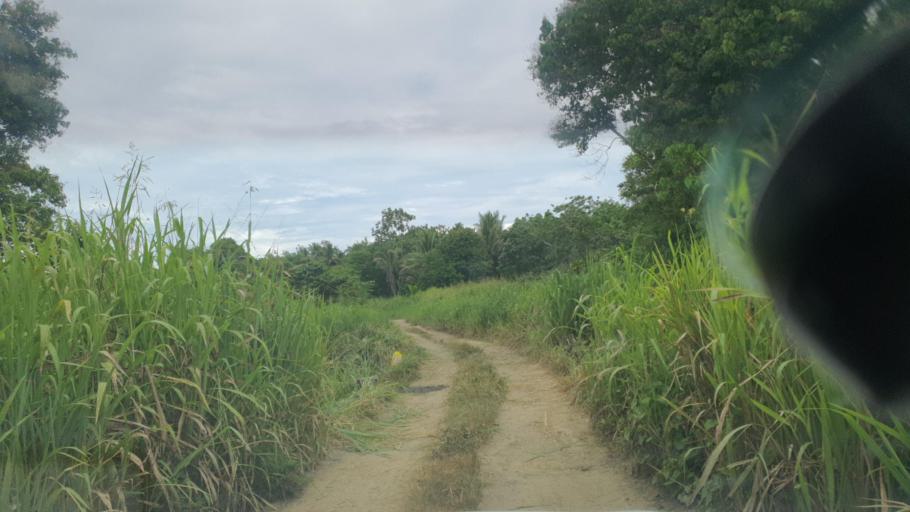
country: SB
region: Guadalcanal
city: Honiara
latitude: -9.4910
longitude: 160.3409
